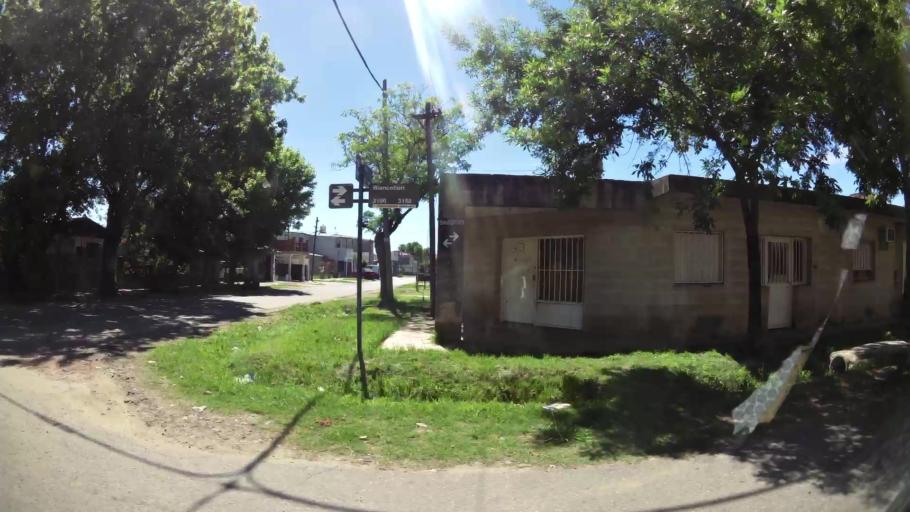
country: AR
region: Santa Fe
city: Perez
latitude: -32.9652
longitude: -60.7141
